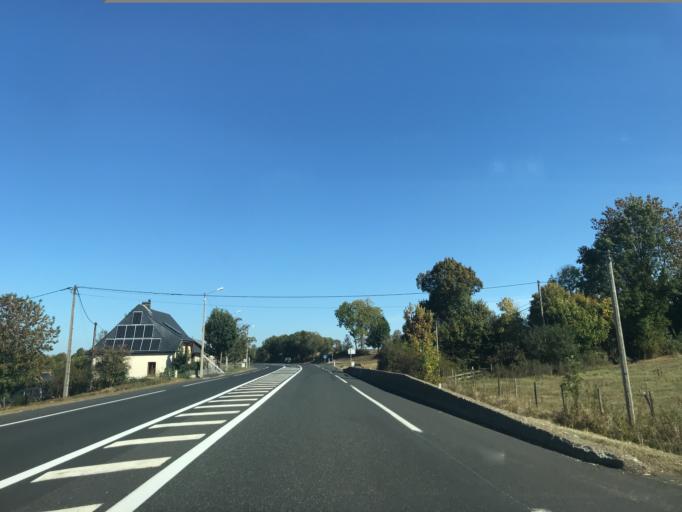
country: FR
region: Auvergne
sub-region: Departement du Puy-de-Dome
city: Gelles
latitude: 45.7023
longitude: 2.8086
